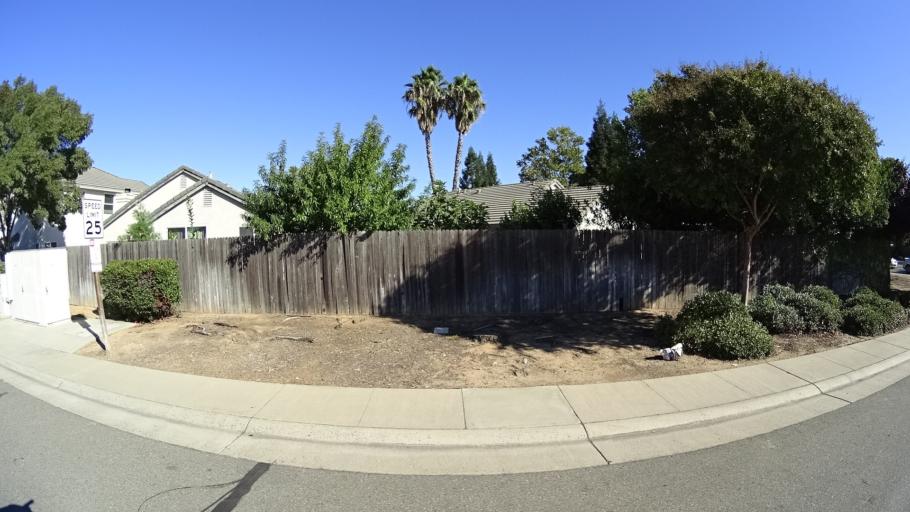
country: US
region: California
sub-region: Sacramento County
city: Vineyard
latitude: 38.4453
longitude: -121.3721
